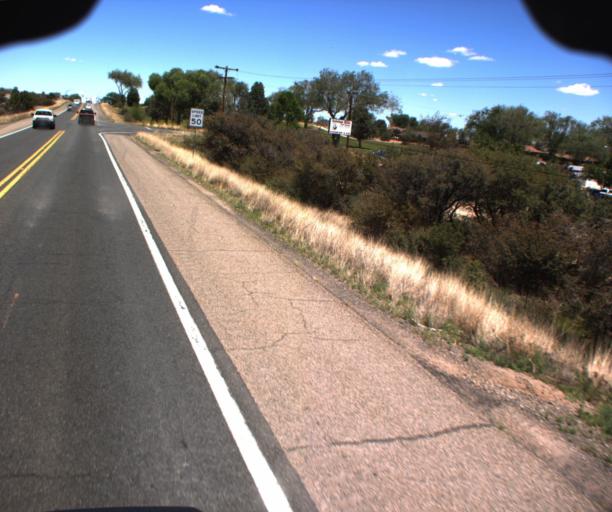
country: US
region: Arizona
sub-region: Yavapai County
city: Prescott
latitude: 34.6392
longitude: -112.4311
